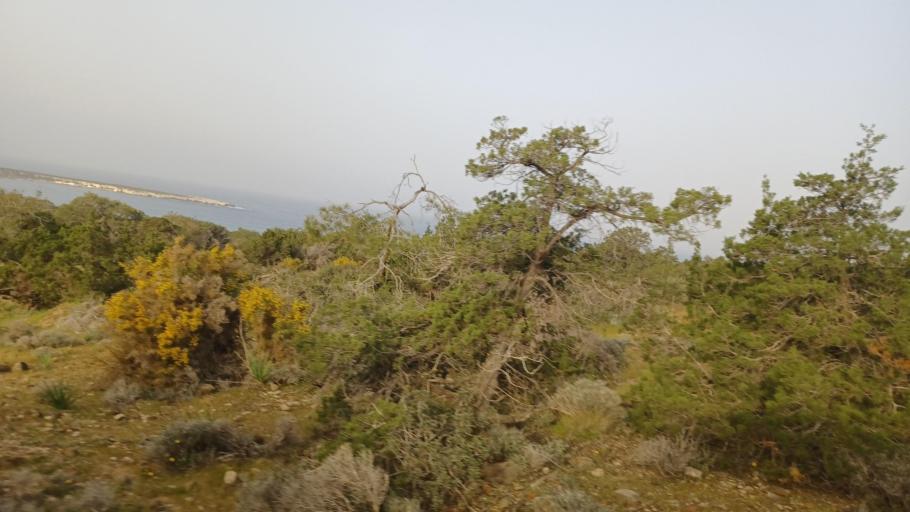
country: CY
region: Pafos
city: Pegeia
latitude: 34.9681
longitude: 32.3161
